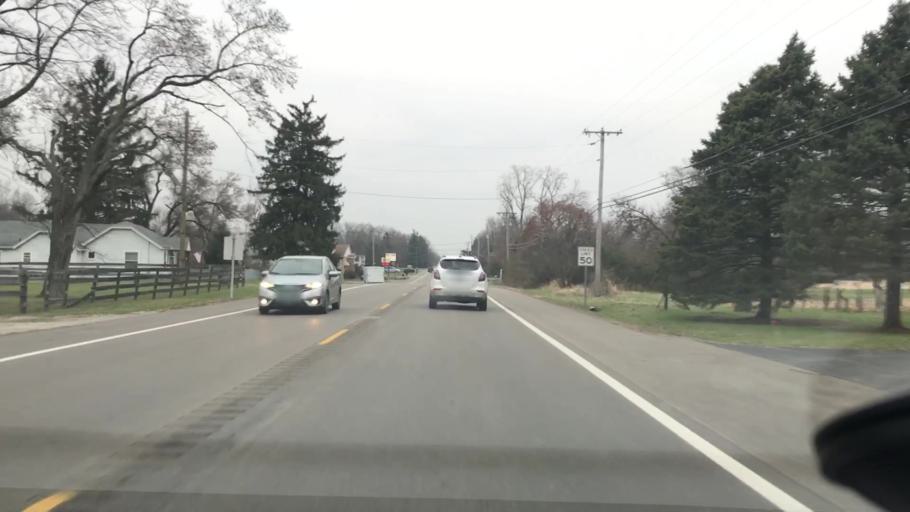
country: US
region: Ohio
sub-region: Greene County
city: Yellow Springs
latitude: 39.8373
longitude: -83.8653
